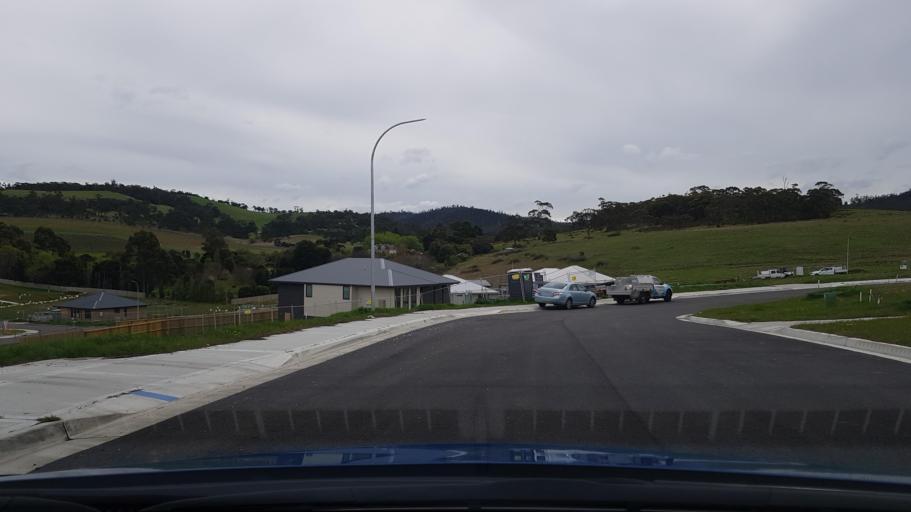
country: AU
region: Tasmania
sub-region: Clarence
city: Howrah
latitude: -42.8788
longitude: 147.4301
